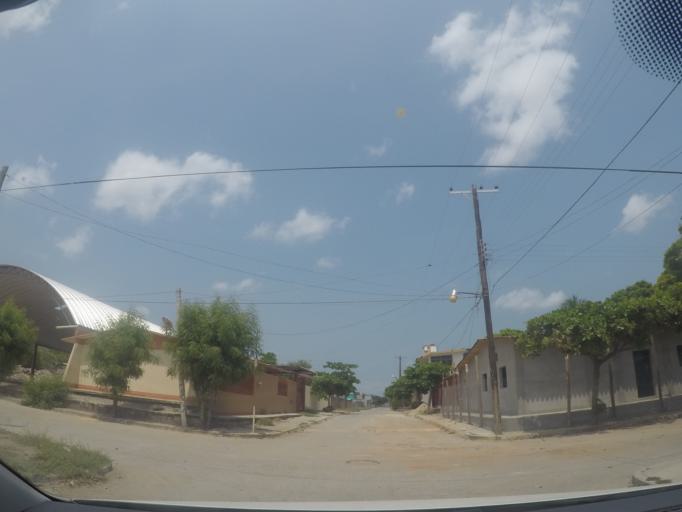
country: MX
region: Oaxaca
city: Asuncion Ixtaltepec
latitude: 16.5000
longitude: -95.0629
